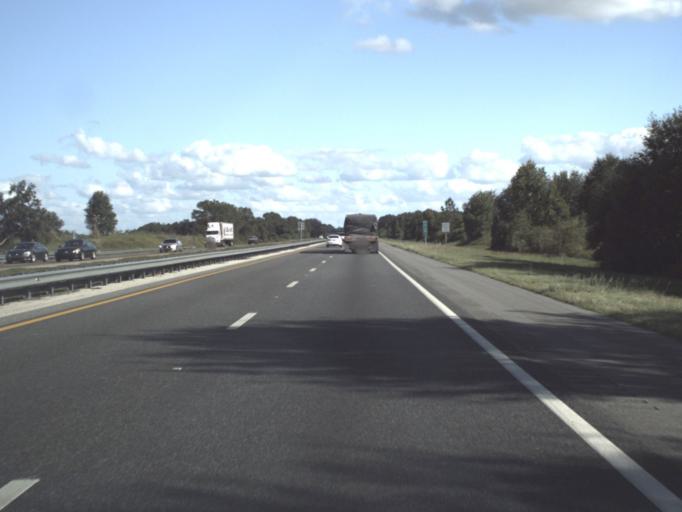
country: US
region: Florida
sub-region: Lake County
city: Howie In The Hills
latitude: 28.6587
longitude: -81.8207
